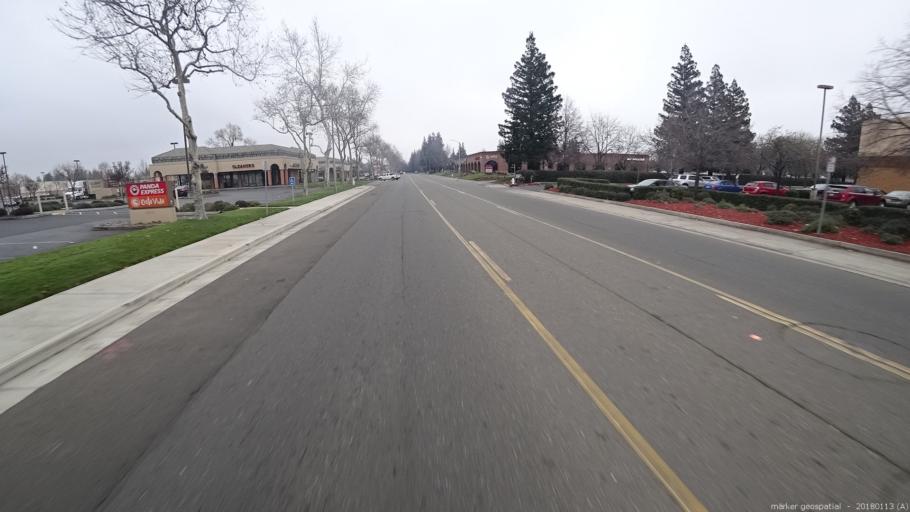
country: US
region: California
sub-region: Sacramento County
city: Rancho Cordova
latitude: 38.5939
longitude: -121.2852
